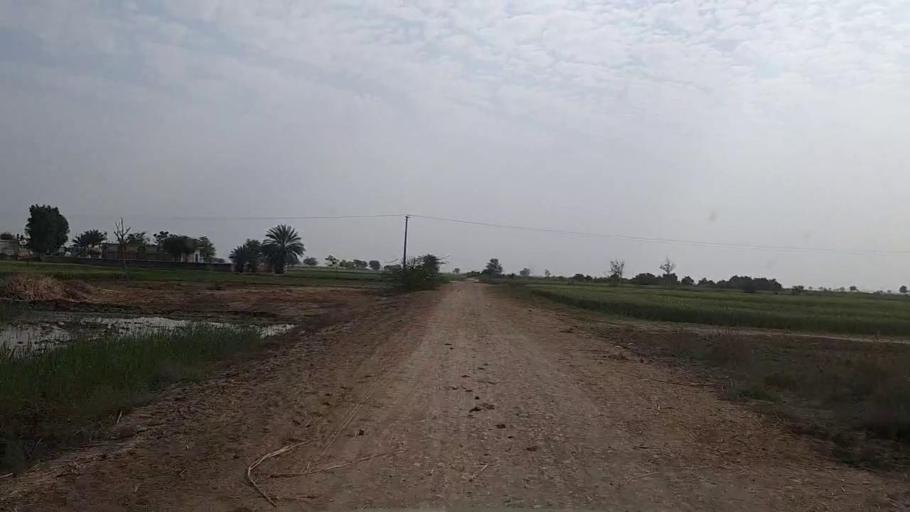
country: PK
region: Sindh
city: Mirwah Gorchani
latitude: 25.3930
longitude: 69.1018
